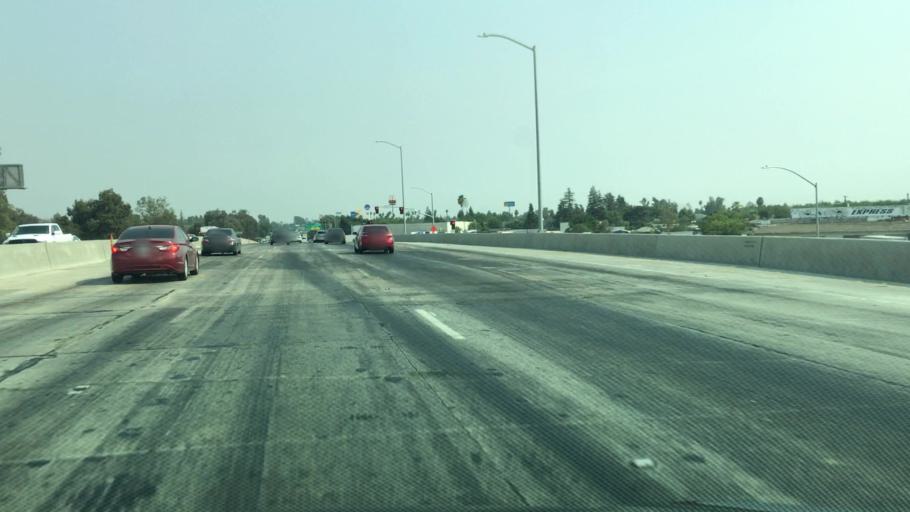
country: US
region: California
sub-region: Fresno County
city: West Park
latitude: 36.7650
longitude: -119.8344
